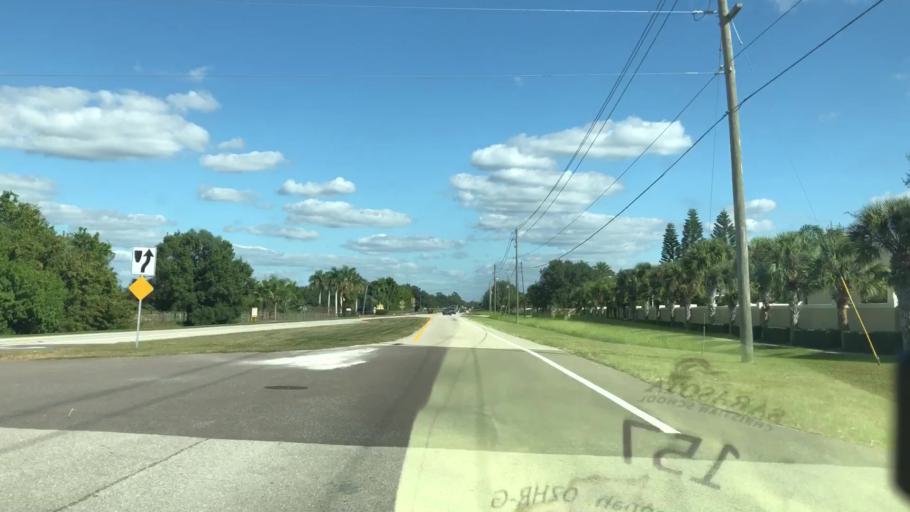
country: US
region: Florida
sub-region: Sarasota County
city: Fruitville
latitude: 27.3249
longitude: -82.4318
